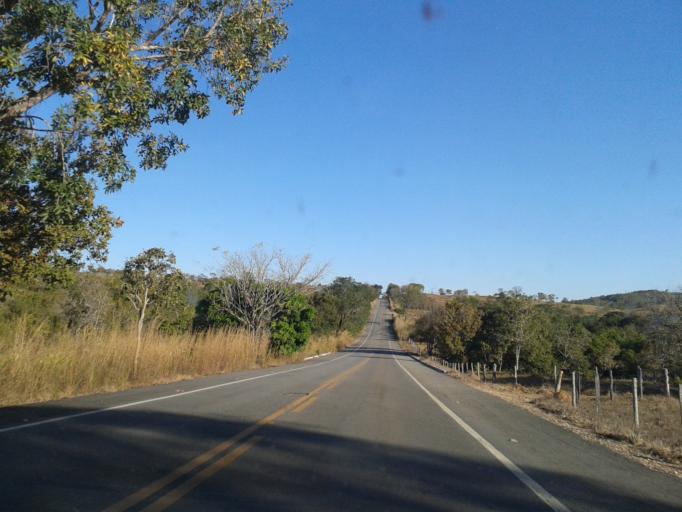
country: BR
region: Goias
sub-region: Itapuranga
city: Itapuranga
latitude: -15.6446
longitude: -50.2245
